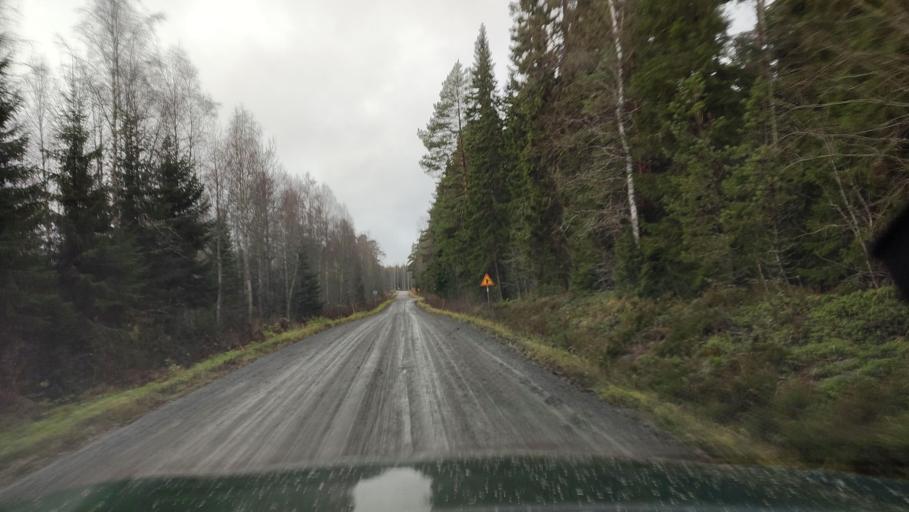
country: FI
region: Ostrobothnia
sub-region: Sydosterbotten
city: Naerpes
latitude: 62.4584
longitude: 21.4959
